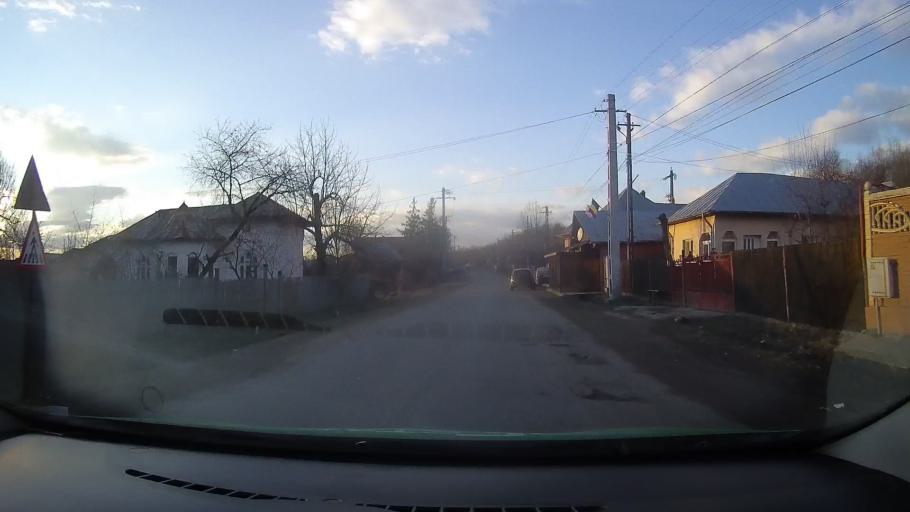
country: RO
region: Dambovita
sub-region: Comuna Gura Ocnitei
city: Adanca
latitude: 44.9212
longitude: 25.6130
